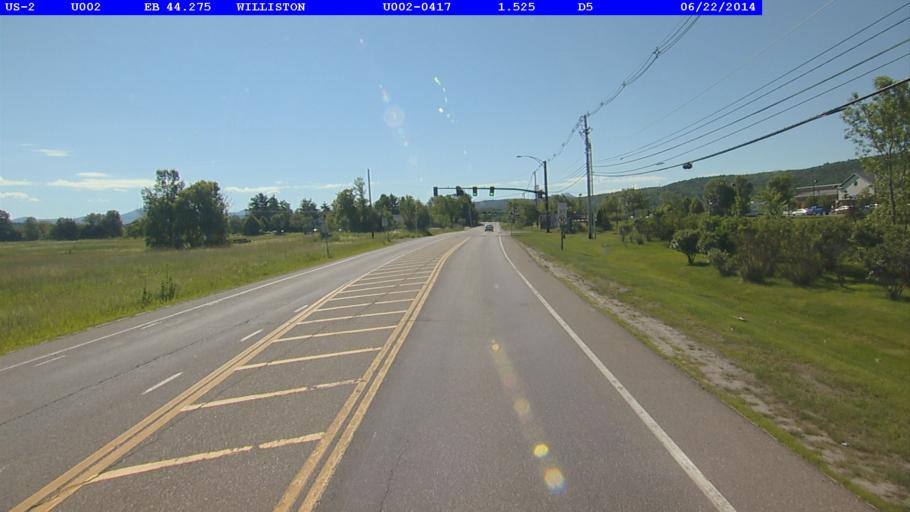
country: US
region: Vermont
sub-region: Chittenden County
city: Essex Junction
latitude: 44.4488
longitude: -73.1092
